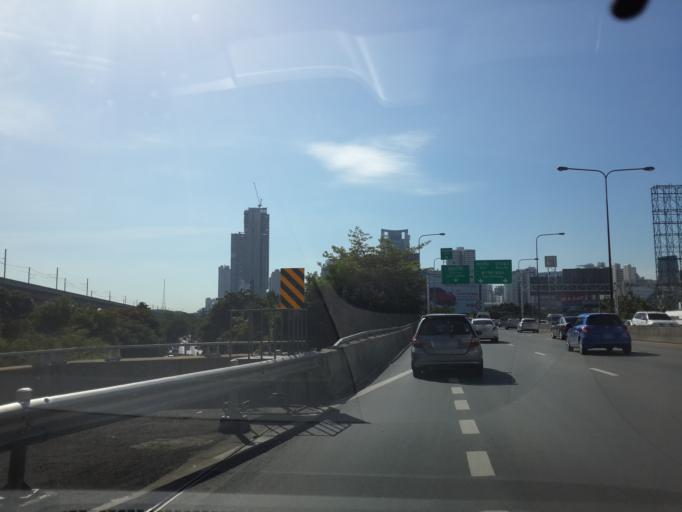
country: TH
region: Bangkok
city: Ratchathewi
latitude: 13.7534
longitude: 100.5473
